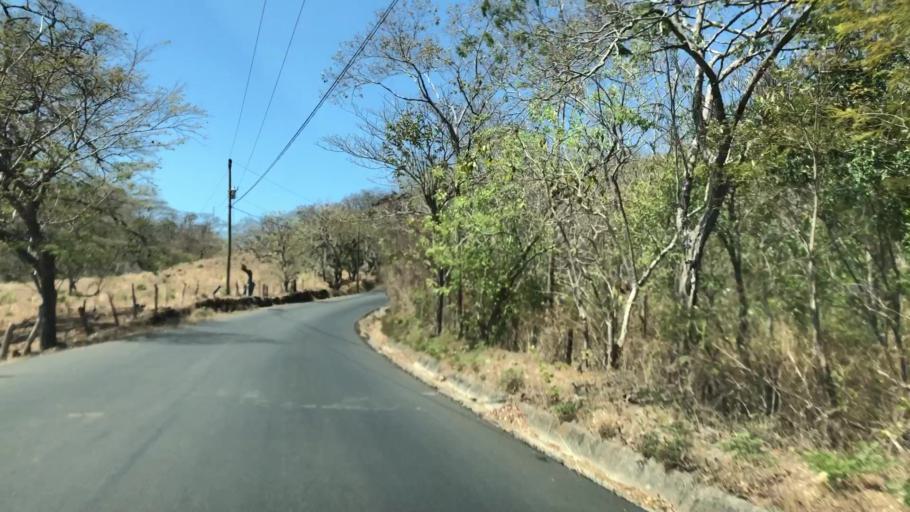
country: CR
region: Guanacaste
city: Belen
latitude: 10.3499
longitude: -85.8202
